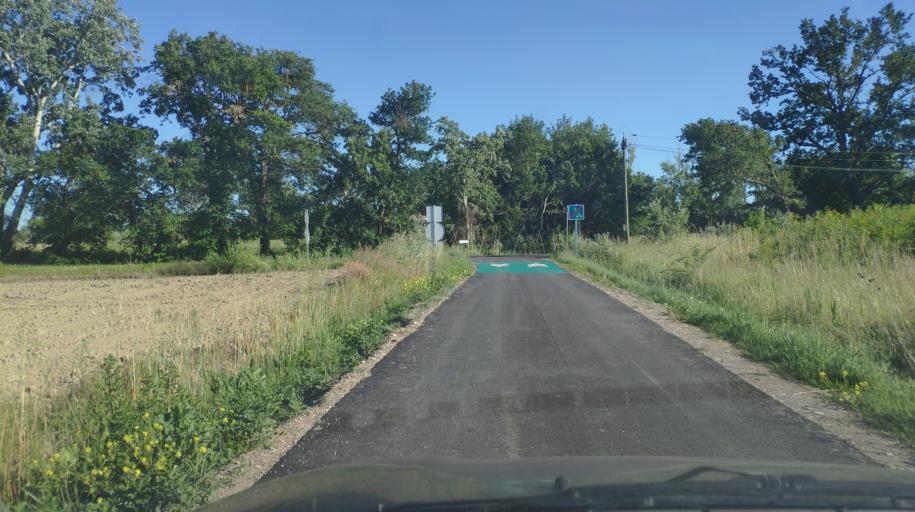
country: FR
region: Provence-Alpes-Cote d'Azur
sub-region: Departement du Vaucluse
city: Piolenc
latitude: 44.1696
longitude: 4.7479
